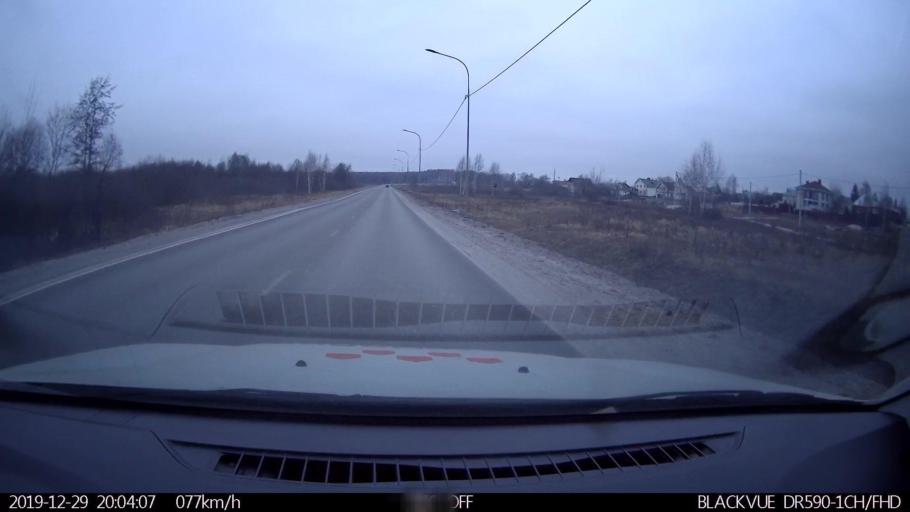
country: RU
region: Nizjnij Novgorod
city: Neklyudovo
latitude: 56.3803
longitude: 44.0099
